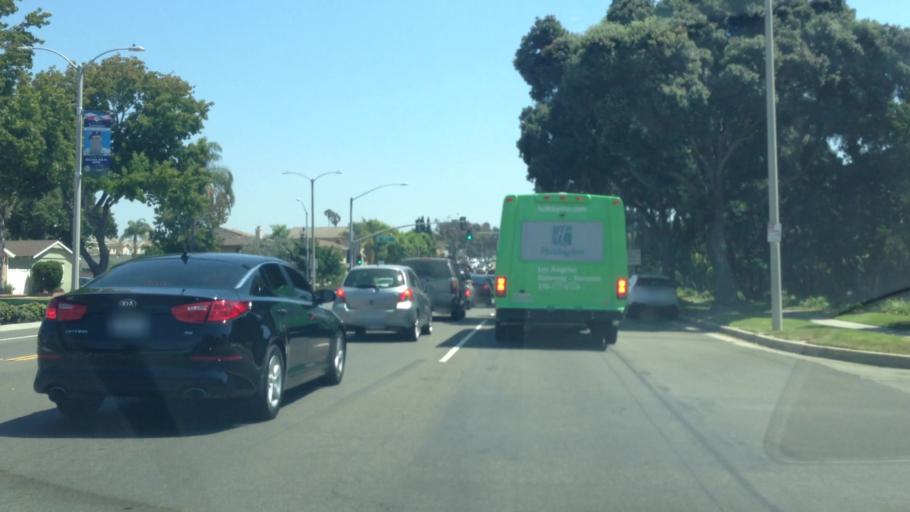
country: US
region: California
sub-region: Los Angeles County
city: Torrance
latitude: 33.8312
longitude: -118.3410
